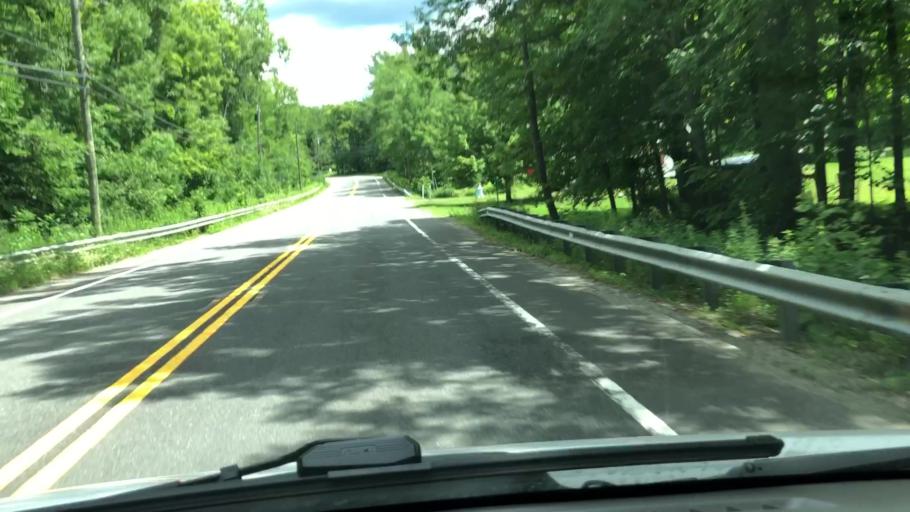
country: US
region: Massachusetts
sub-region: Berkshire County
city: Adams
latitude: 42.5835
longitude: -73.0812
